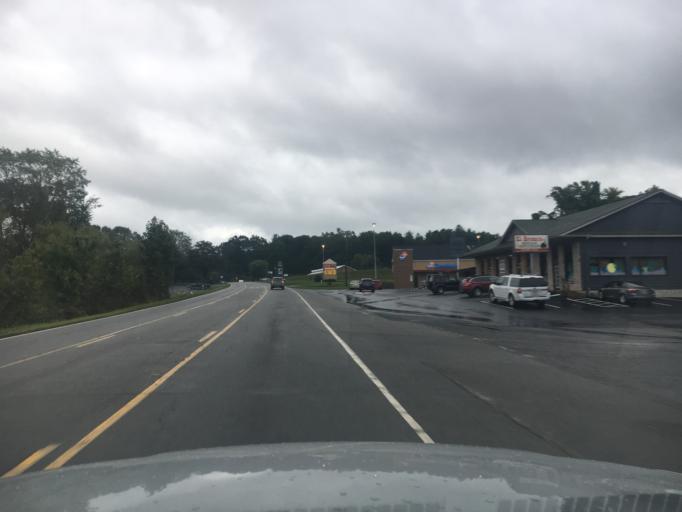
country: US
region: North Carolina
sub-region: Henderson County
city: Etowah
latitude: 35.3178
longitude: -82.5918
